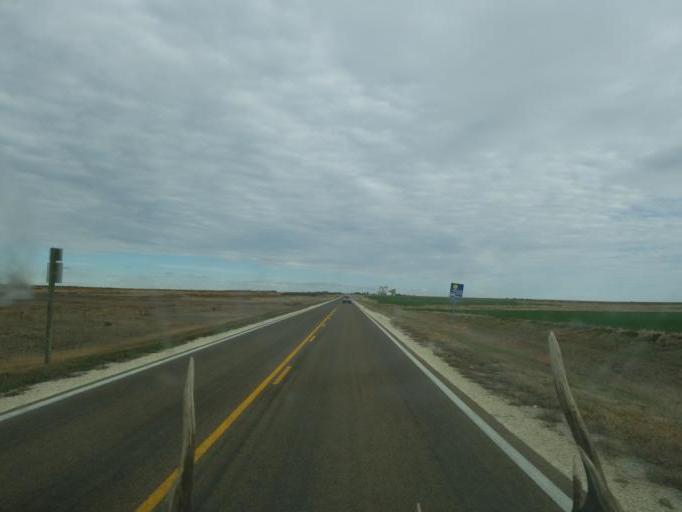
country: US
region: Kansas
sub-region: Logan County
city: Oakley
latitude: 39.0816
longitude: -101.1804
